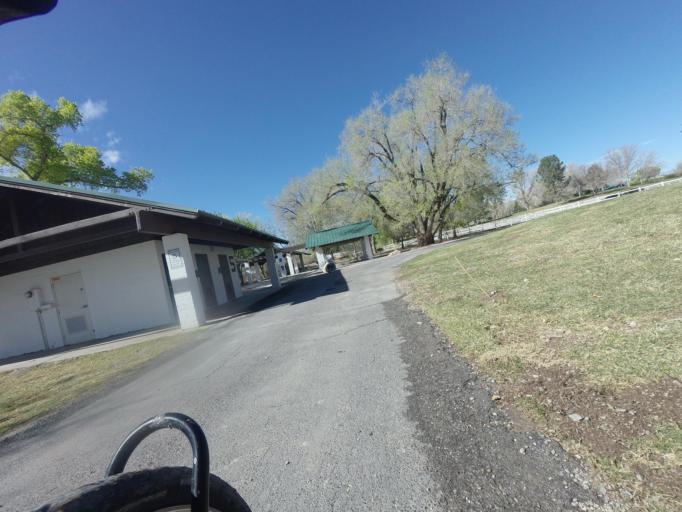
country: US
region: Nevada
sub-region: Clark County
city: North Las Vegas
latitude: 36.3244
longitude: -115.2628
